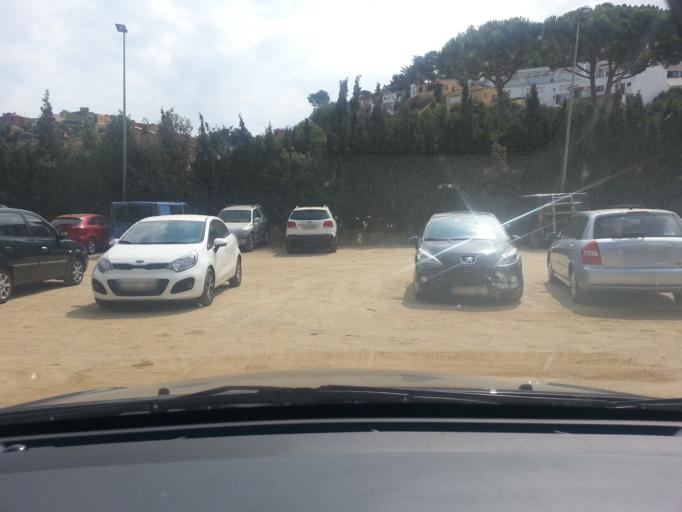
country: ES
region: Catalonia
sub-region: Provincia de Girona
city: Begur
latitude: 41.9575
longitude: 3.2056
